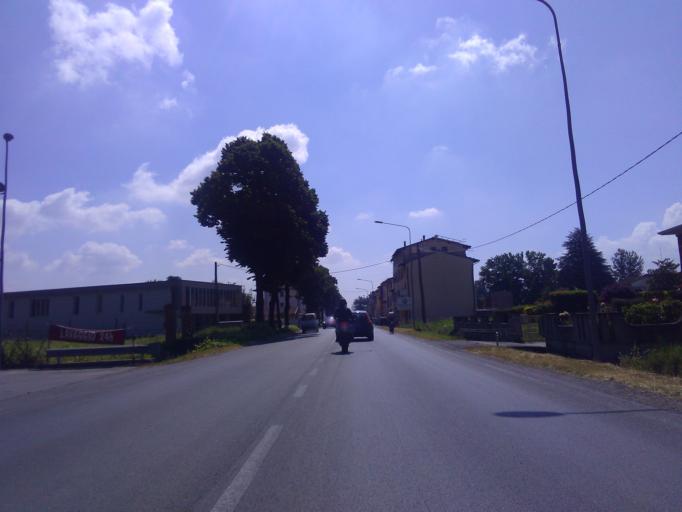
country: IT
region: Tuscany
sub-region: Provincia di Lucca
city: Lucca
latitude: 43.8498
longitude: 10.4610
